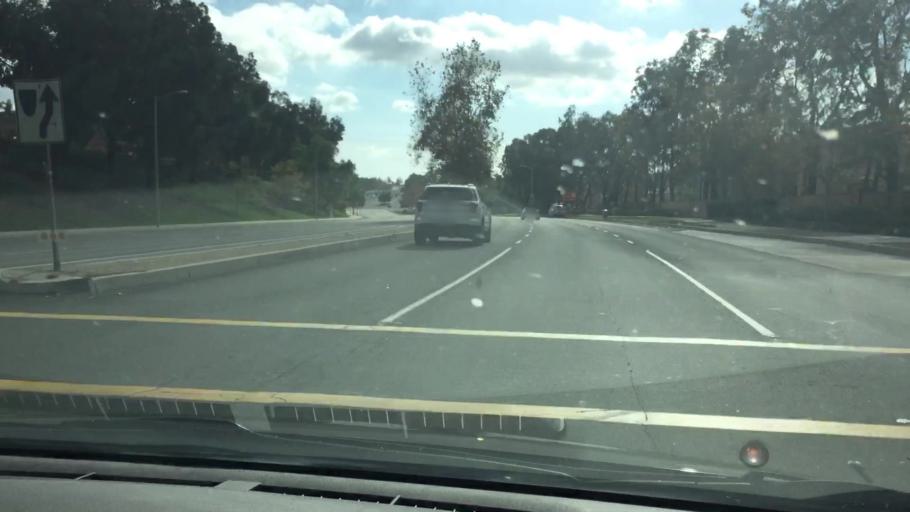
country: US
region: California
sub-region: Orange County
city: Las Flores
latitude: 33.5878
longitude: -117.6296
